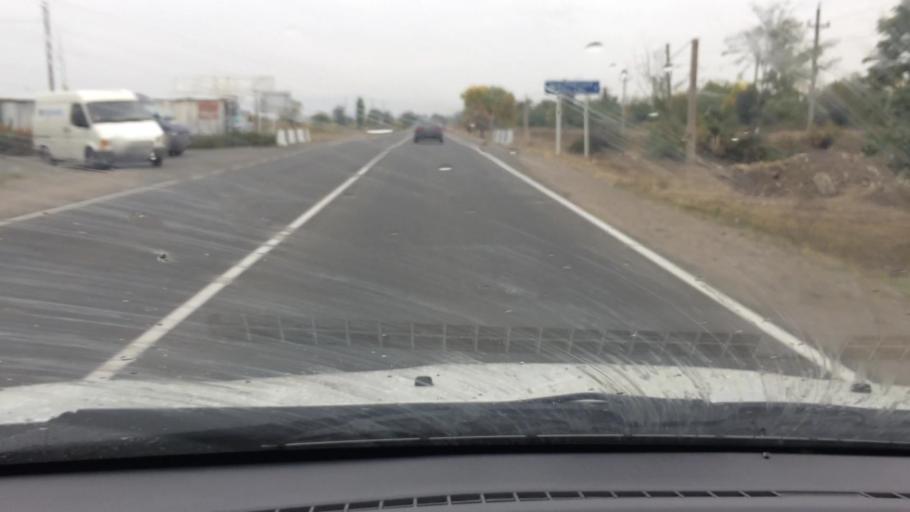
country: GE
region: Kvemo Kartli
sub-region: Marneuli
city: Marneuli
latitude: 41.4219
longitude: 44.8245
